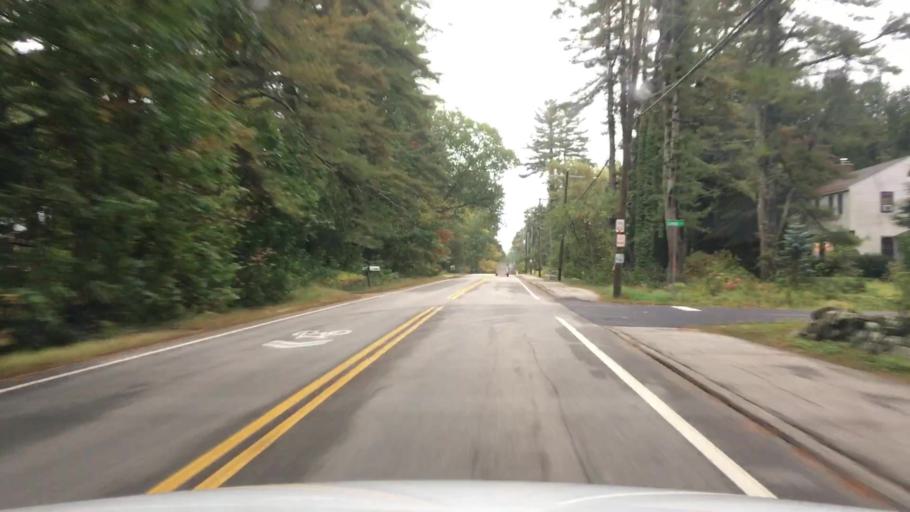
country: US
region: New Hampshire
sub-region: Strafford County
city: Durham
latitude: 43.1505
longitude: -70.9300
